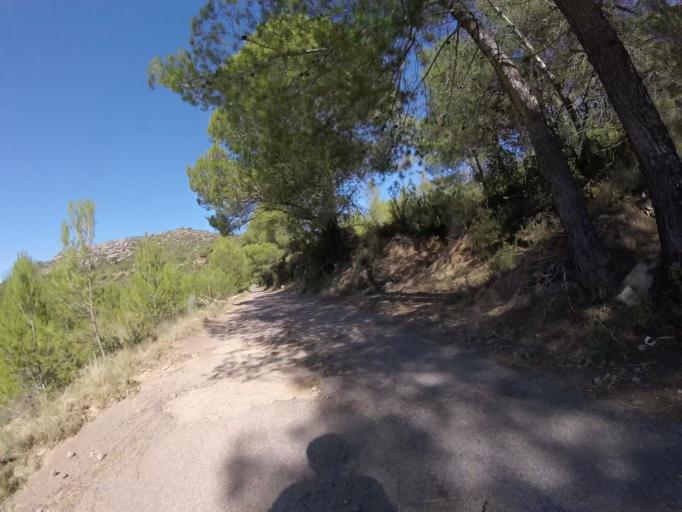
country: ES
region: Valencia
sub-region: Provincia de Castello
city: Orpesa/Oropesa del Mar
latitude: 40.1389
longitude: 0.1025
